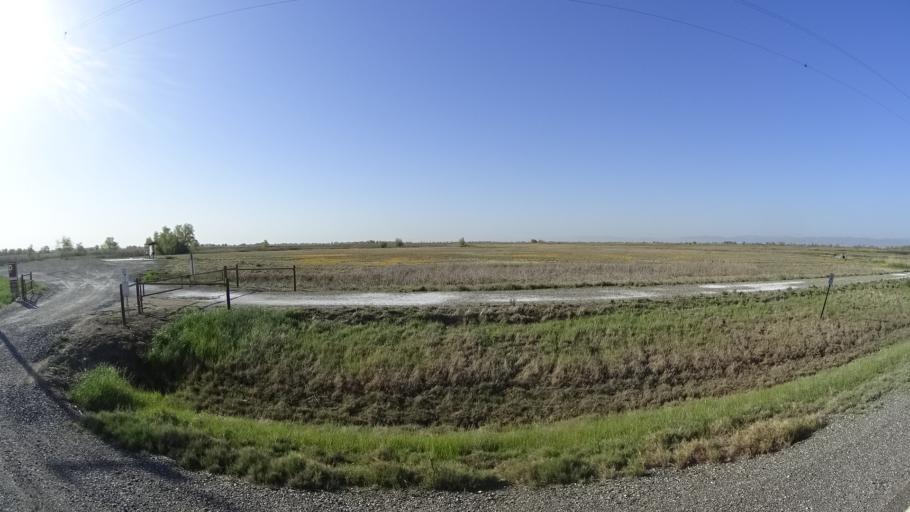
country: US
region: California
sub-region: Glenn County
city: Willows
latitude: 39.4074
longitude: -122.1451
